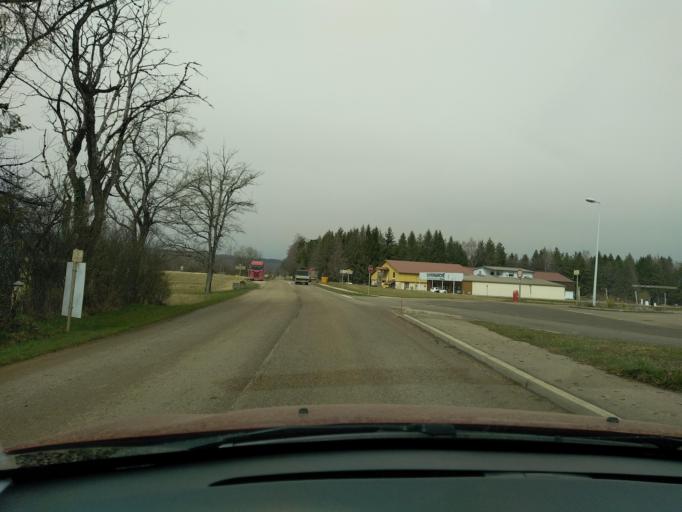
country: FR
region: Franche-Comte
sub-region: Departement du Jura
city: Clairvaux-les-Lacs
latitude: 46.6608
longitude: 5.7758
